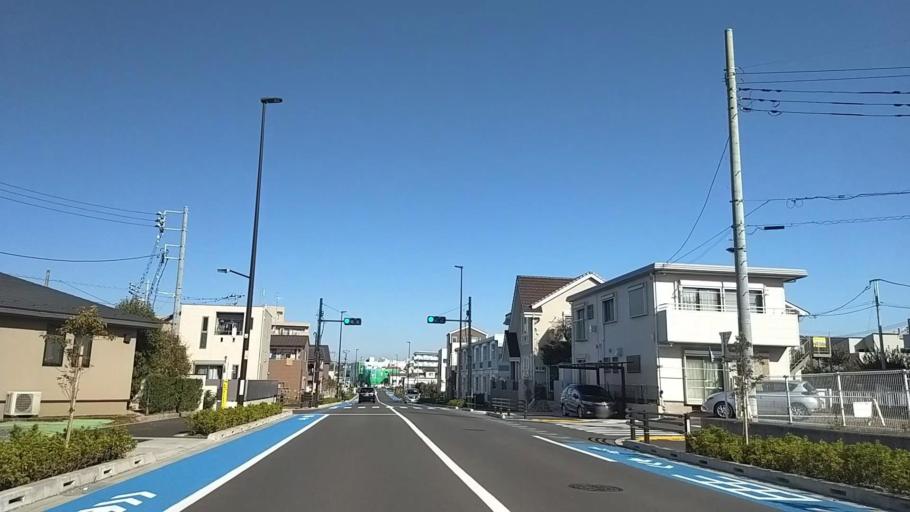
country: JP
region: Tokyo
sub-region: Machida-shi
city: Machida
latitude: 35.5155
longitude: 139.4652
